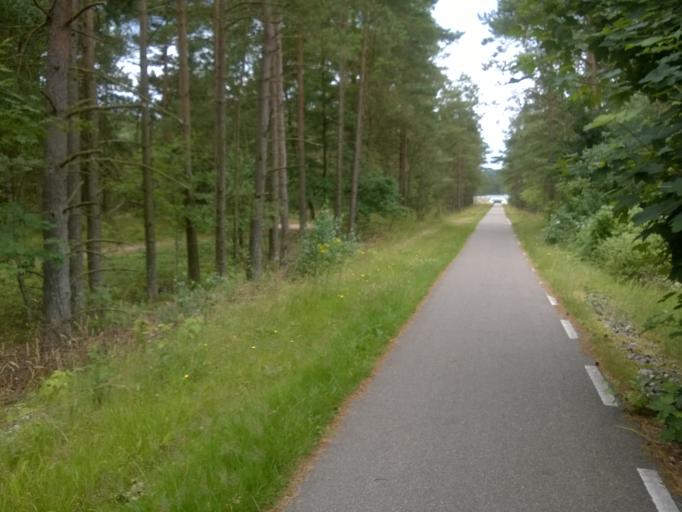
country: DK
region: Central Jutland
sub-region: Silkeborg Kommune
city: Svejbaek
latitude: 56.1688
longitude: 9.6082
